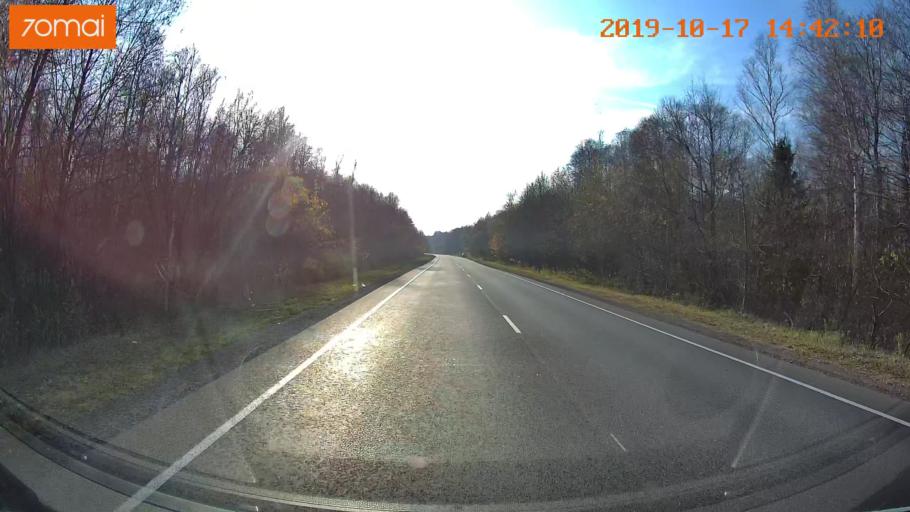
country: RU
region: Rjazan
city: Solotcha
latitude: 54.8398
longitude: 39.9295
